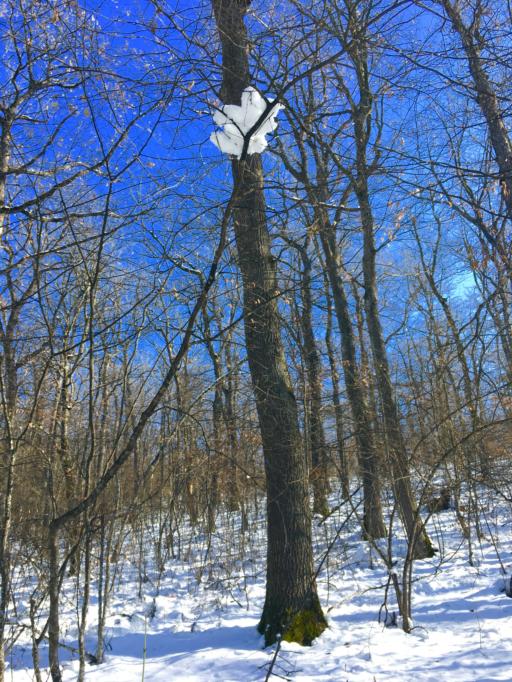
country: XK
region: Pristina
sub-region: Komuna e Prishtines
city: Pristina
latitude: 42.6731
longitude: 21.2216
